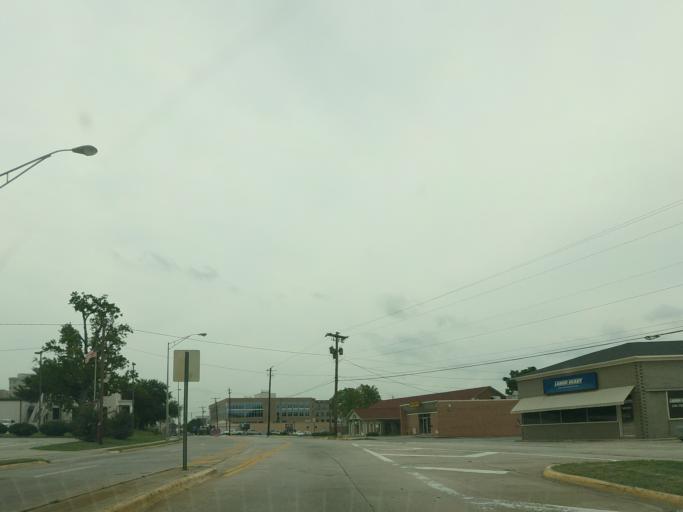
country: US
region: Georgia
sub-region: Bibb County
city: Macon
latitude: 32.8302
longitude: -83.6369
